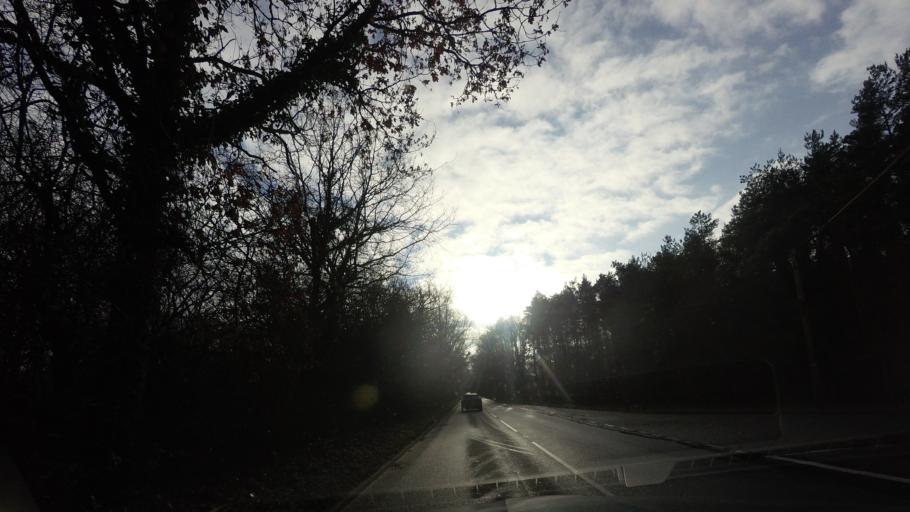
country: GB
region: England
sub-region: East Sussex
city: Battle
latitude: 50.9481
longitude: 0.4832
